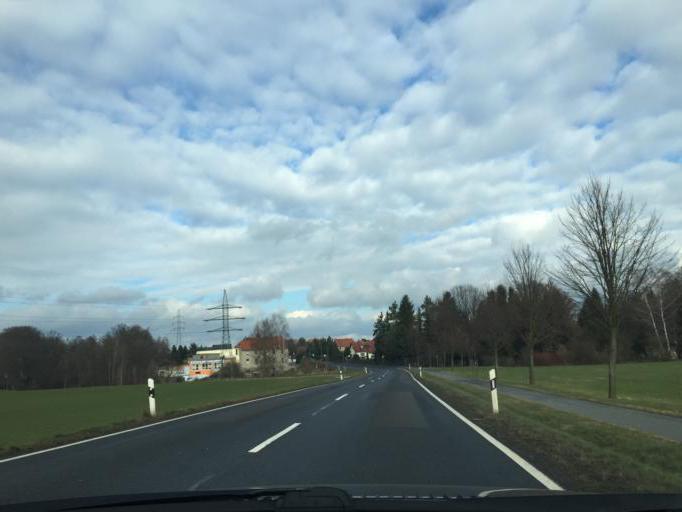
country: DE
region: Saxony
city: Radeberg
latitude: 51.1341
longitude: 13.9164
